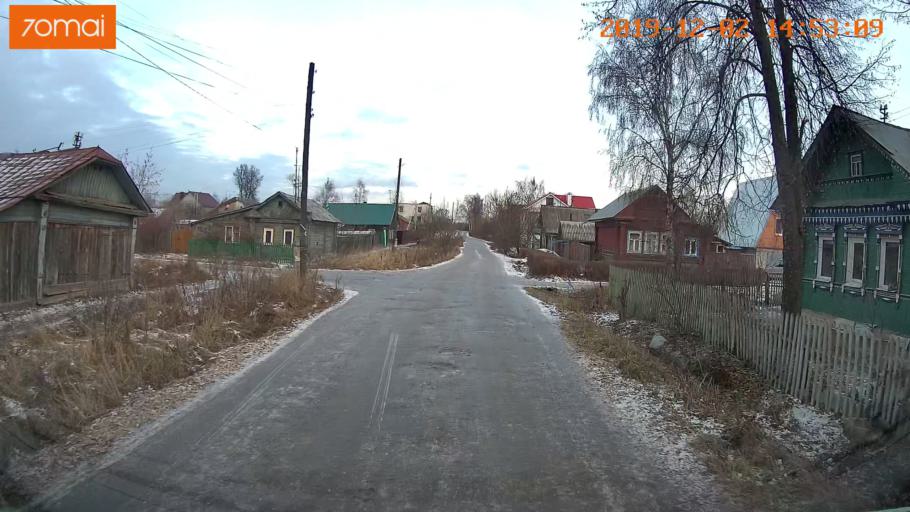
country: RU
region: Ivanovo
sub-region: Gorod Ivanovo
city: Ivanovo
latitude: 56.9750
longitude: 41.0133
